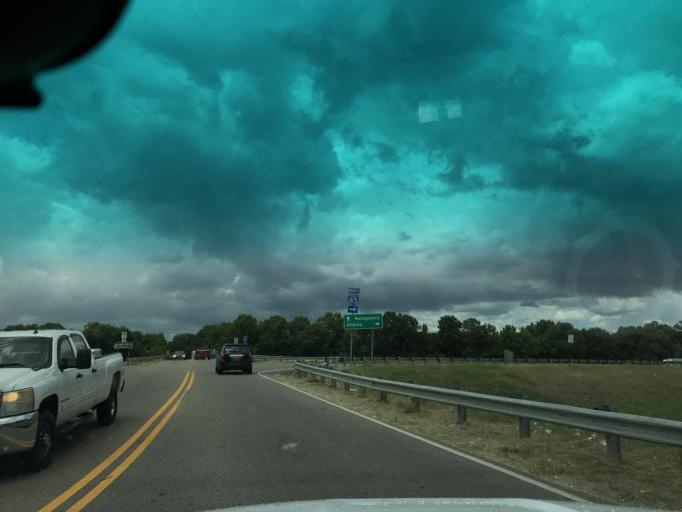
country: US
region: Alabama
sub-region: Montgomery County
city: Pike Road
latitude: 32.3675
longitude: -86.0523
